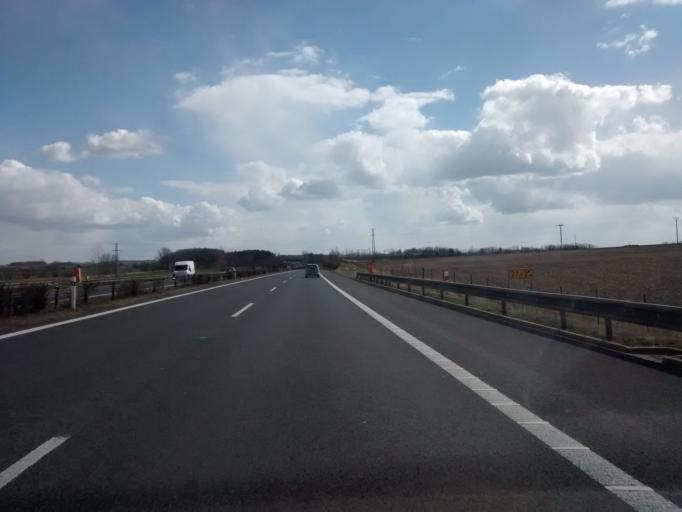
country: CZ
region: Ustecky
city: Roudnice nad Labem
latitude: 50.3796
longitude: 14.2462
